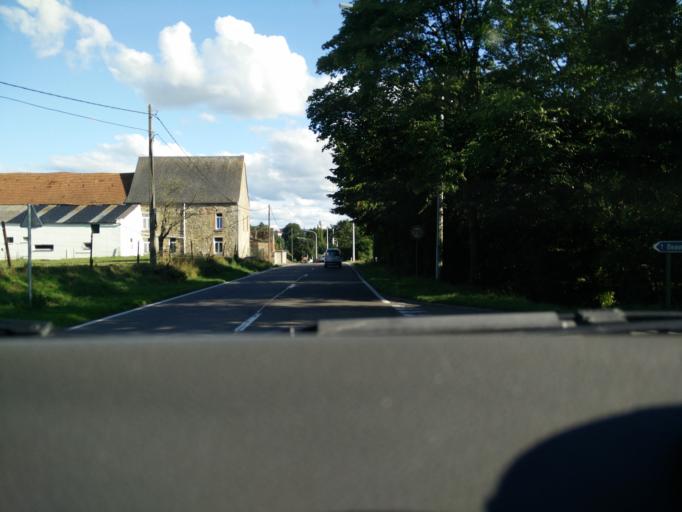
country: BE
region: Wallonia
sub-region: Province du Hainaut
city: Beaumont
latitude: 50.2438
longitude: 4.2327
